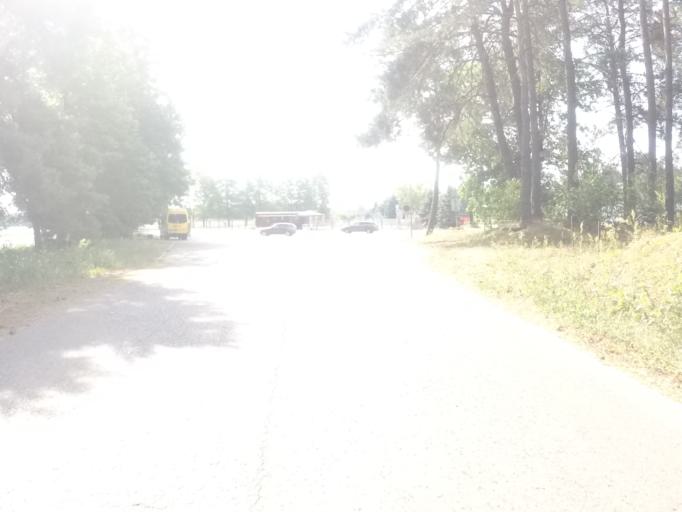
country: LT
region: Alytaus apskritis
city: Druskininkai
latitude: 54.0253
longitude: 24.0780
